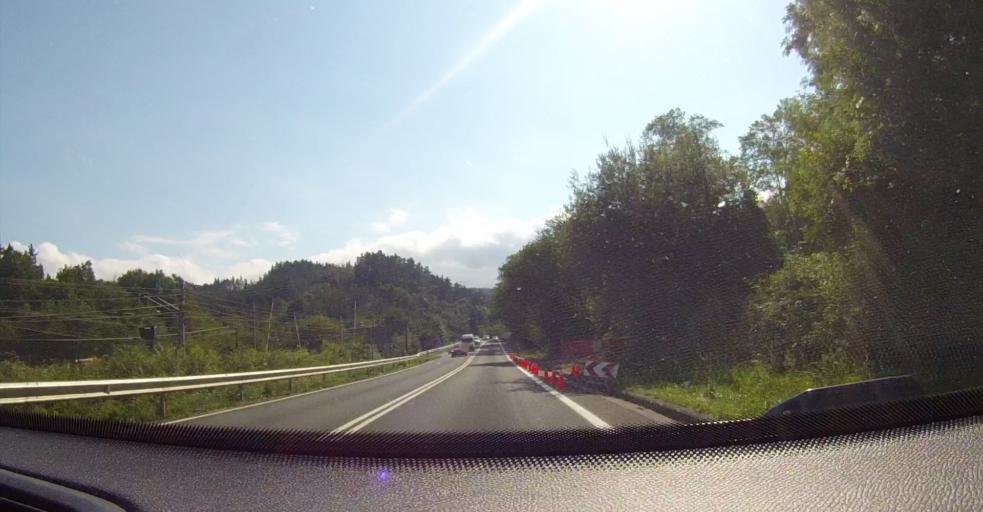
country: ES
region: Basque Country
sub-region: Bizkaia
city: Muxika
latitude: 43.2507
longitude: -2.6958
